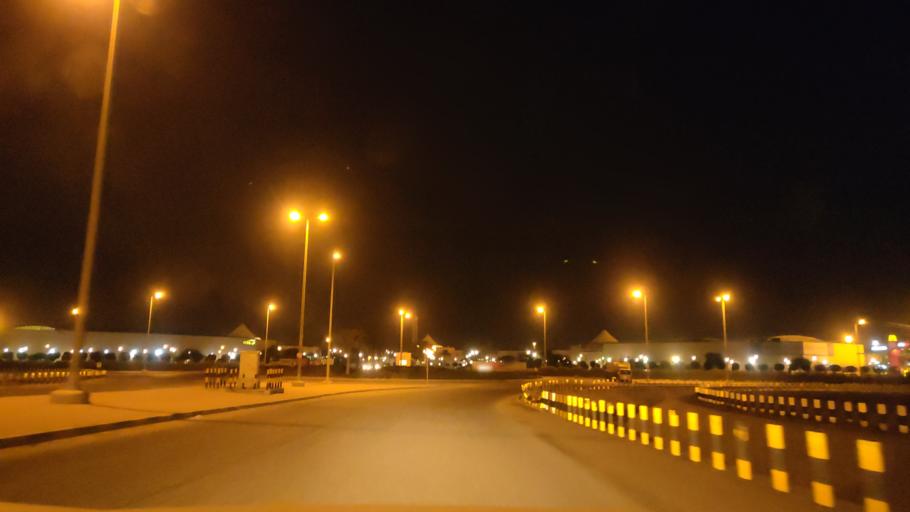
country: KW
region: Al Asimah
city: Ar Rabiyah
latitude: 29.2510
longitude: 47.8445
